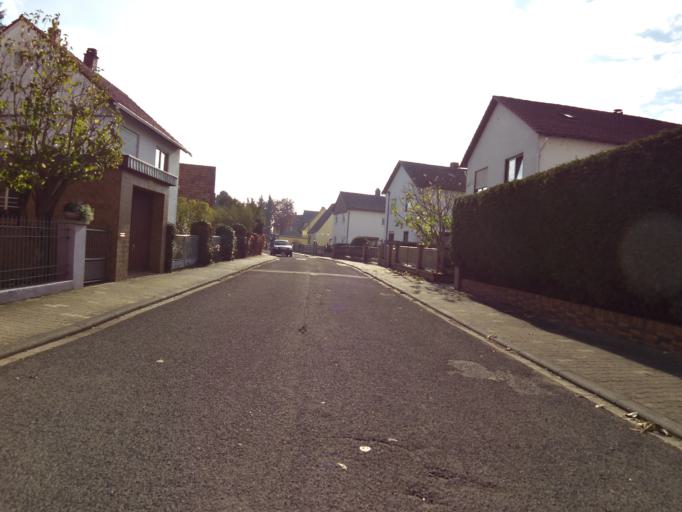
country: DE
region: Rheinland-Pfalz
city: Dirmstein
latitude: 49.5606
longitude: 8.2432
